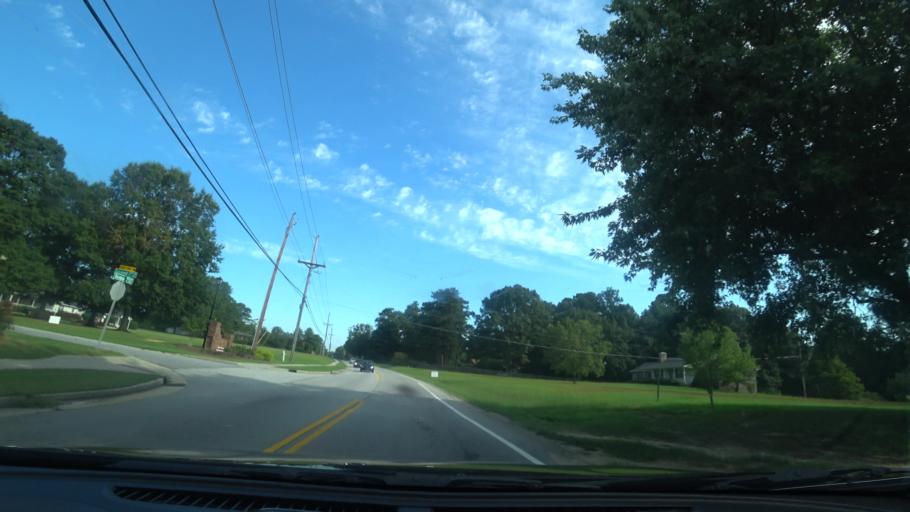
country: US
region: Georgia
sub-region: Gwinnett County
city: Grayson
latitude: 33.8805
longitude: -83.9565
